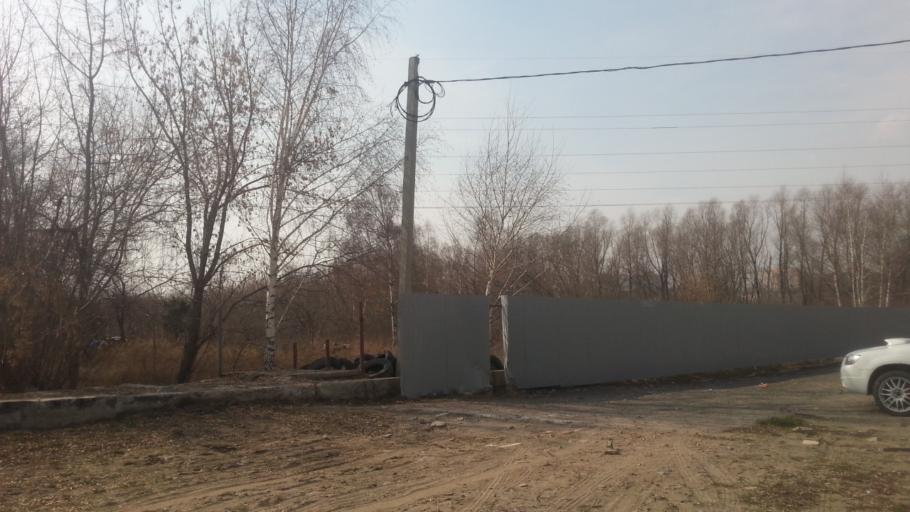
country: RU
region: Altai Krai
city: Zaton
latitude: 53.3269
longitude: 83.7926
